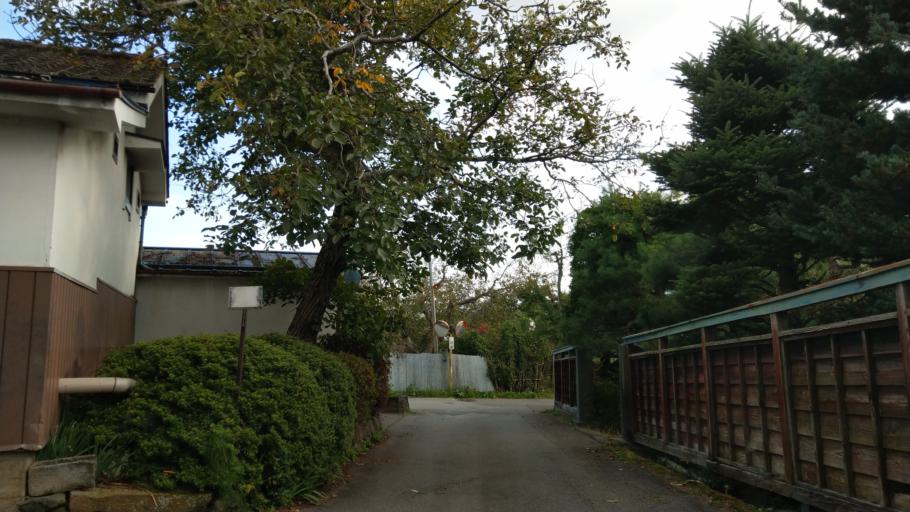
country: JP
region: Nagano
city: Komoro
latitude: 36.3358
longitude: 138.4195
